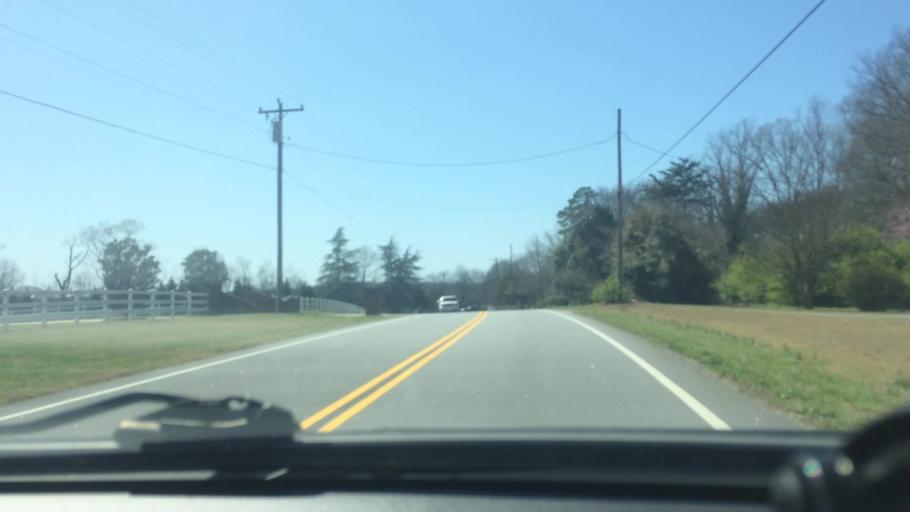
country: US
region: South Carolina
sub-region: Anderson County
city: Powdersville
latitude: 34.7887
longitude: -82.4970
